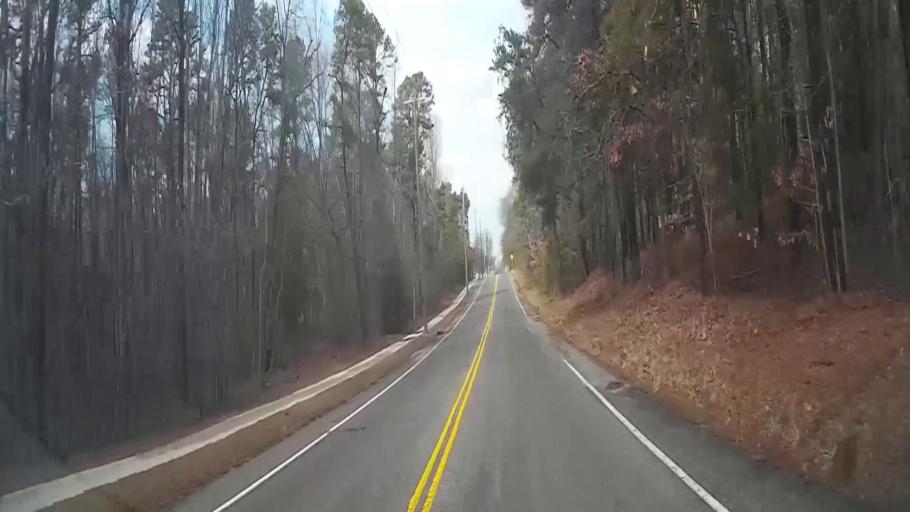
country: US
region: New Jersey
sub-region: Gloucester County
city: Turnersville
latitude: 39.7802
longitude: -75.0339
